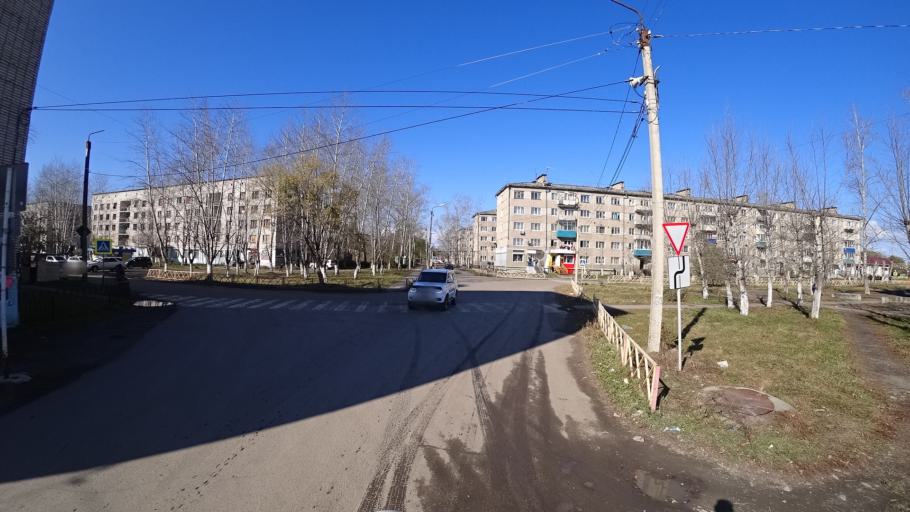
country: RU
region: Khabarovsk Krai
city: Amursk
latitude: 50.0986
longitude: 136.5129
